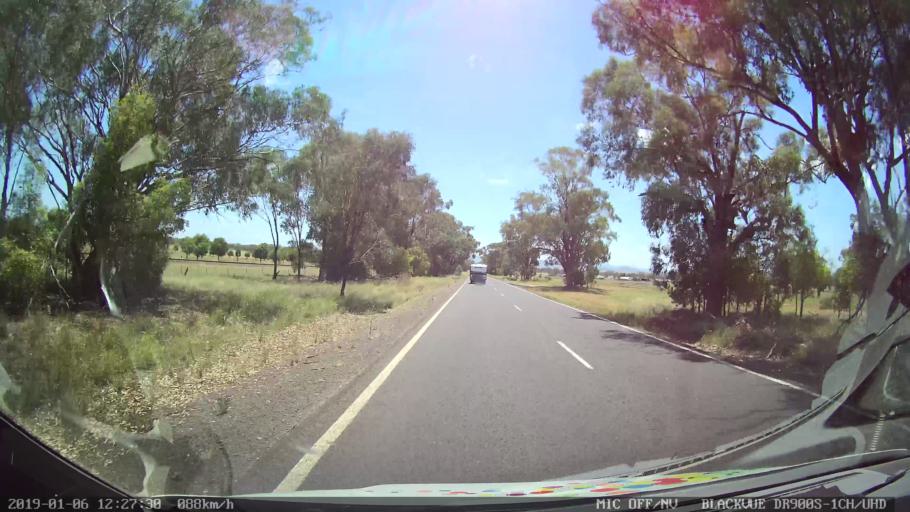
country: AU
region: New South Wales
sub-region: Tamworth Municipality
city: Phillip
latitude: -31.2060
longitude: 150.8286
